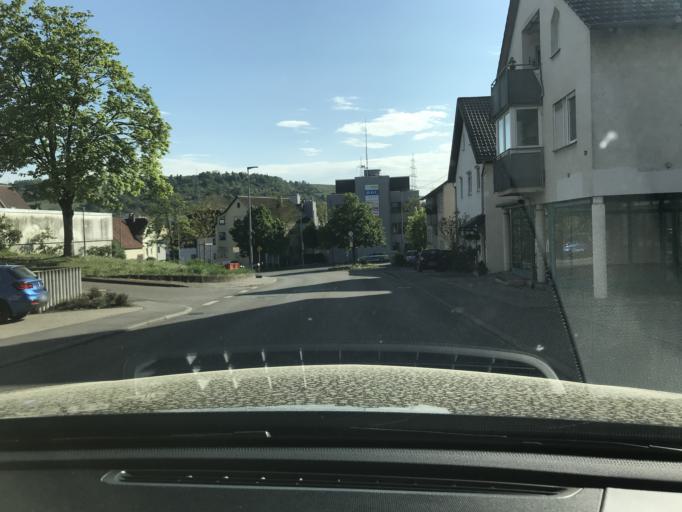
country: DE
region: Baden-Wuerttemberg
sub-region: Regierungsbezirk Stuttgart
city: Weinstadt-Endersbach
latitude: 48.8077
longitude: 9.3862
